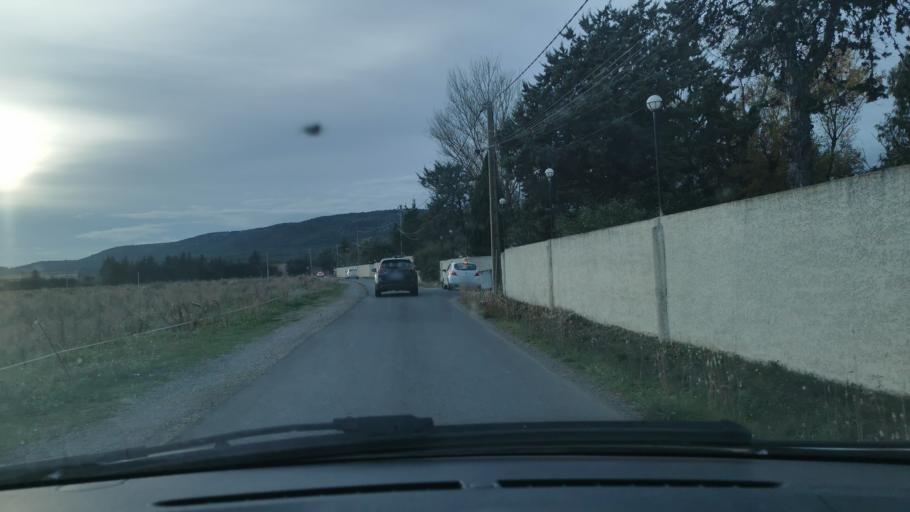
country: FR
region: Languedoc-Roussillon
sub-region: Departement de l'Herault
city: Vic-la-Gardiole
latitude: 43.5004
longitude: 3.7901
